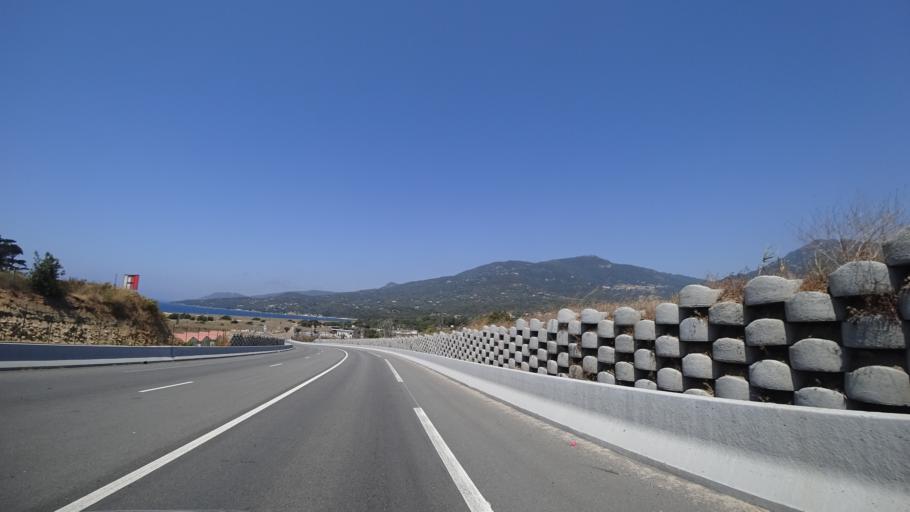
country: FR
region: Corsica
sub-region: Departement de la Corse-du-Sud
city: Propriano
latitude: 41.6831
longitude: 8.9237
